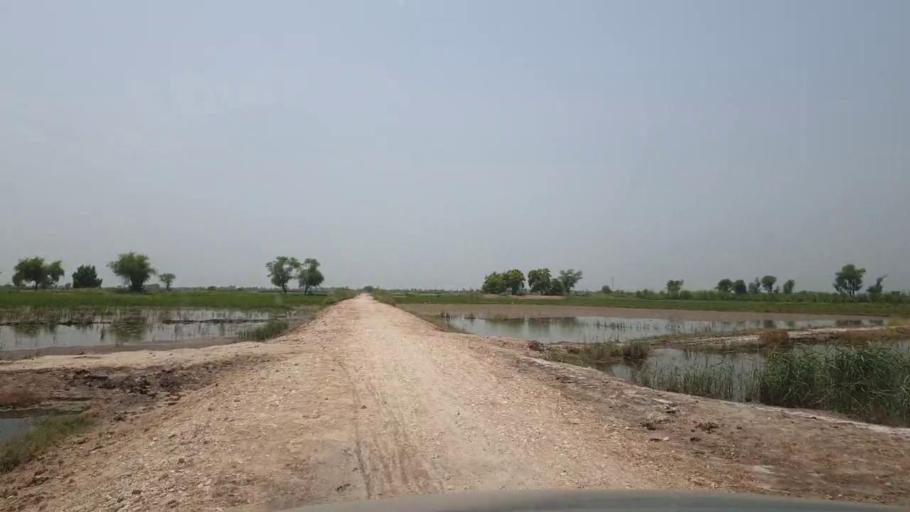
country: PK
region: Sindh
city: Garhi Yasin
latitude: 27.8635
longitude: 68.4824
